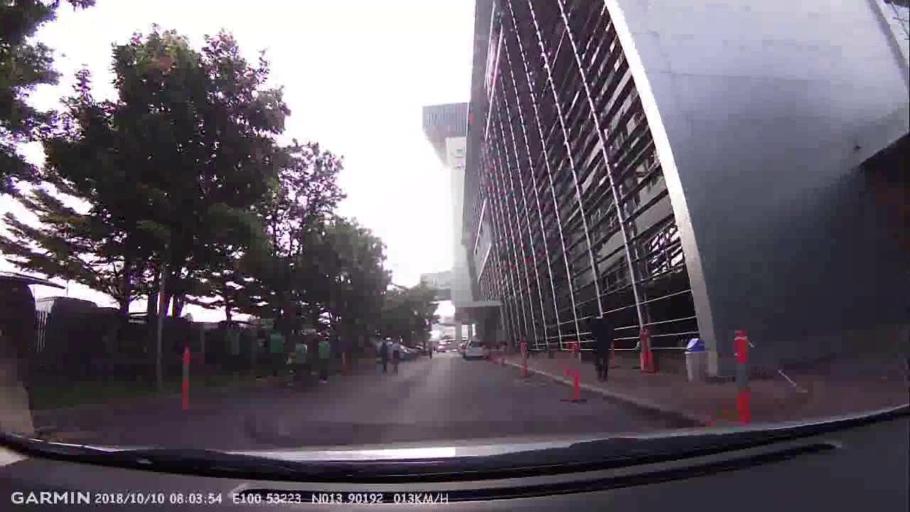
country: TH
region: Nonthaburi
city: Pak Kret
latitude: 13.9019
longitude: 100.5323
